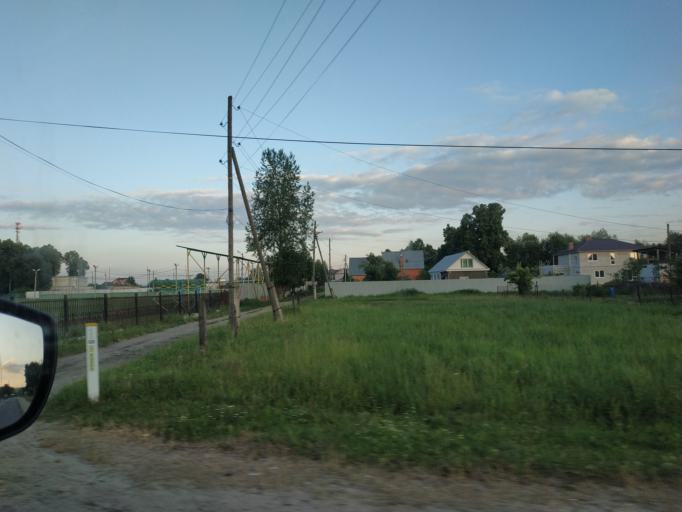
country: RU
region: Moskovskaya
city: Chernogolovka
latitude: 56.0668
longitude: 38.2616
